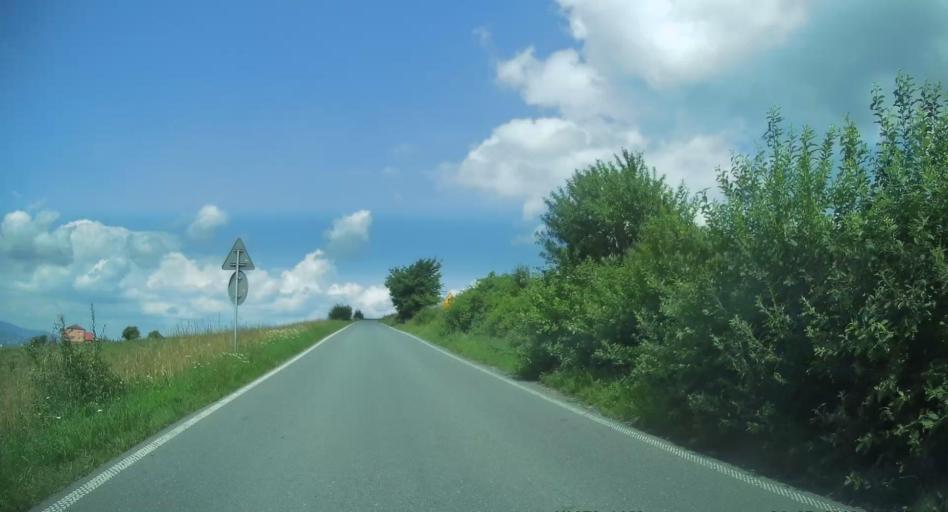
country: PL
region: Lesser Poland Voivodeship
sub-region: Powiat nowosadecki
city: Korzenna
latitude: 49.7057
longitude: 20.7625
